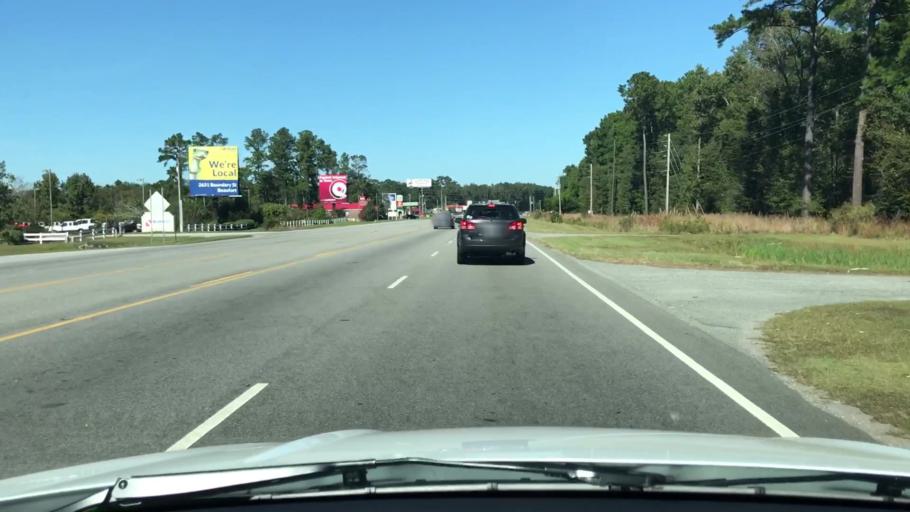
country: US
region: South Carolina
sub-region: Beaufort County
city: Bluffton
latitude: 32.3362
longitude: -80.9283
